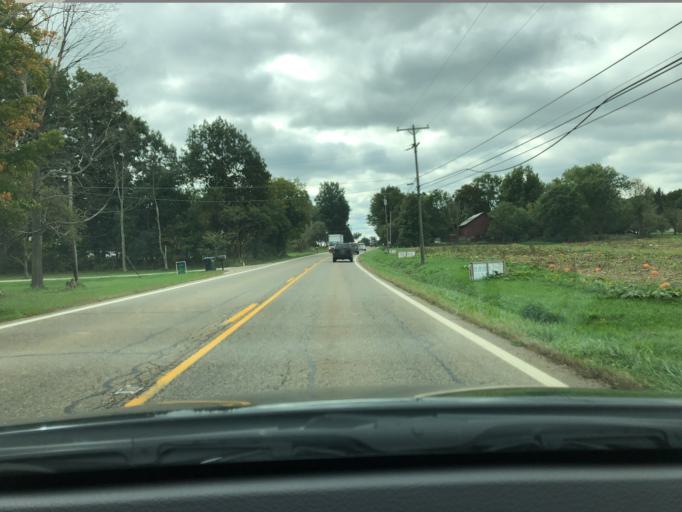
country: US
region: Ohio
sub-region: Stark County
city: Canal Fulton
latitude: 40.8258
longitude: -81.6004
